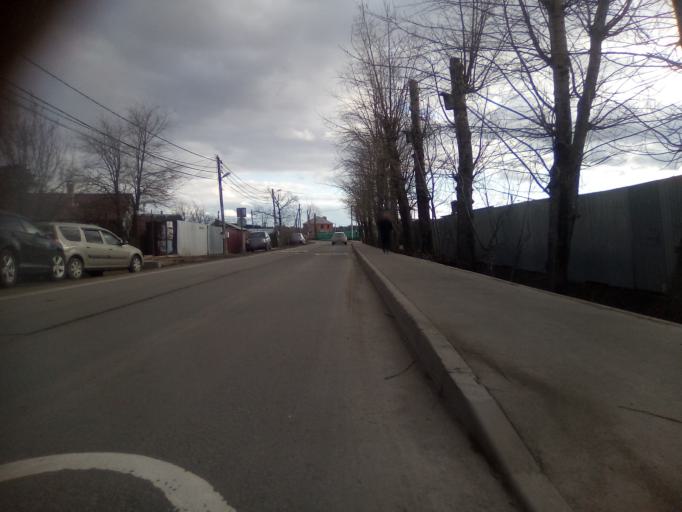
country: RU
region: Moskovskaya
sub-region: Leninskiy Rayon
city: Vnukovo
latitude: 55.5959
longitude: 37.3192
